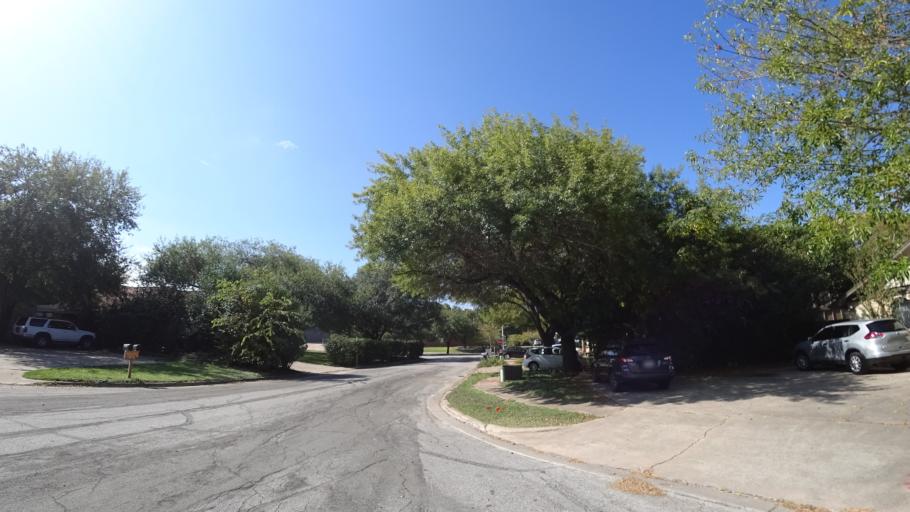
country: US
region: Texas
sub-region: Travis County
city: Shady Hollow
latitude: 30.2100
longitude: -97.8135
